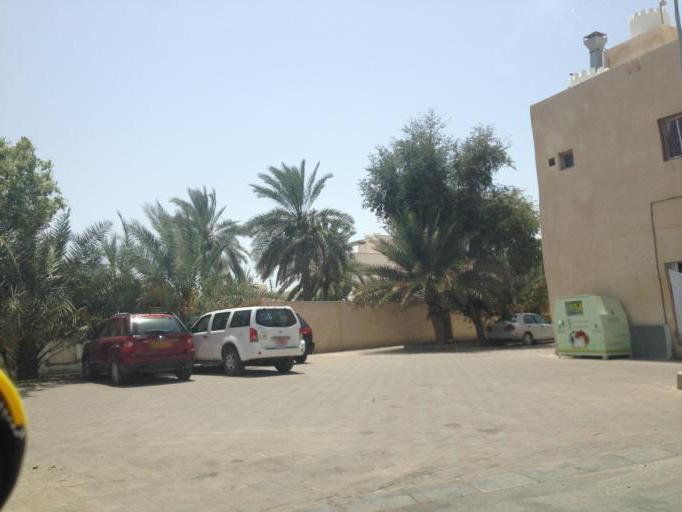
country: OM
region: Muhafazat Masqat
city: As Sib al Jadidah
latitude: 23.6793
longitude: 58.1271
